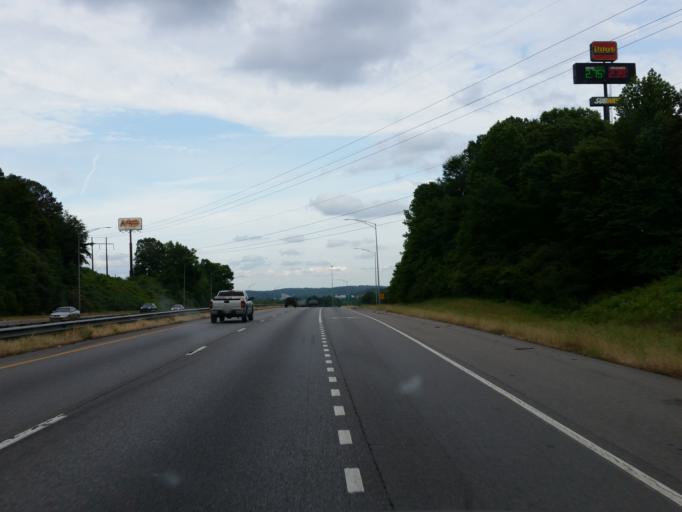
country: US
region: Alabama
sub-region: Tuscaloosa County
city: Holt
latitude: 33.1750
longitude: -87.4817
